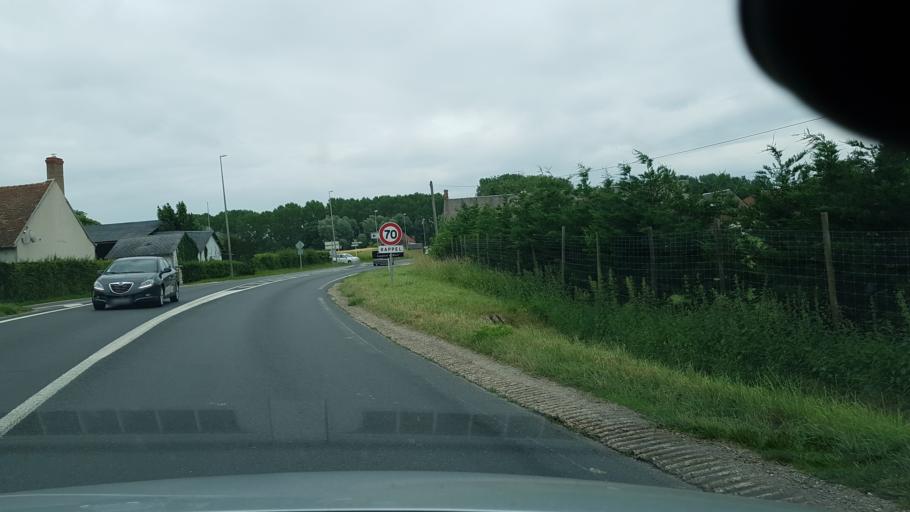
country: FR
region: Centre
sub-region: Departement du Loir-et-Cher
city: Selles-sur-Cher
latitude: 47.2895
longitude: 1.5311
